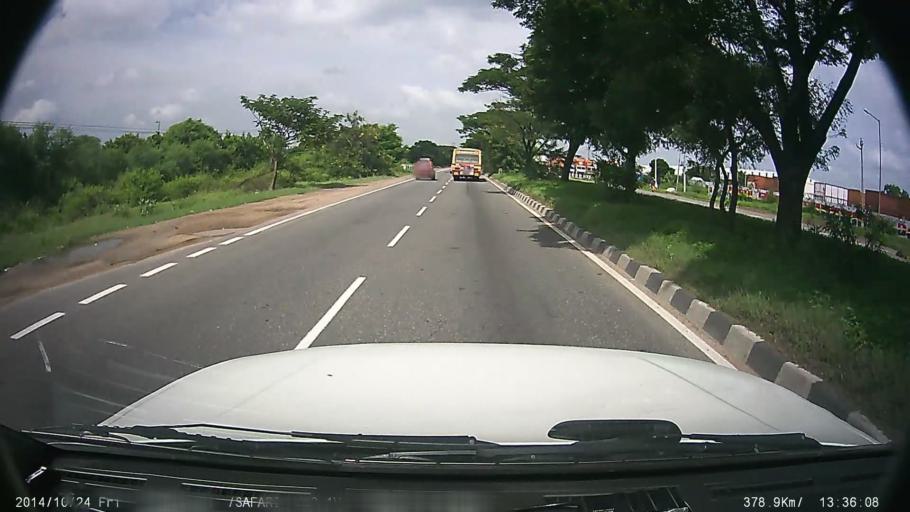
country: IN
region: Tamil Nadu
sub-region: Kancheepuram
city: Singapperumalkovil
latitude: 12.7769
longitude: 80.0103
